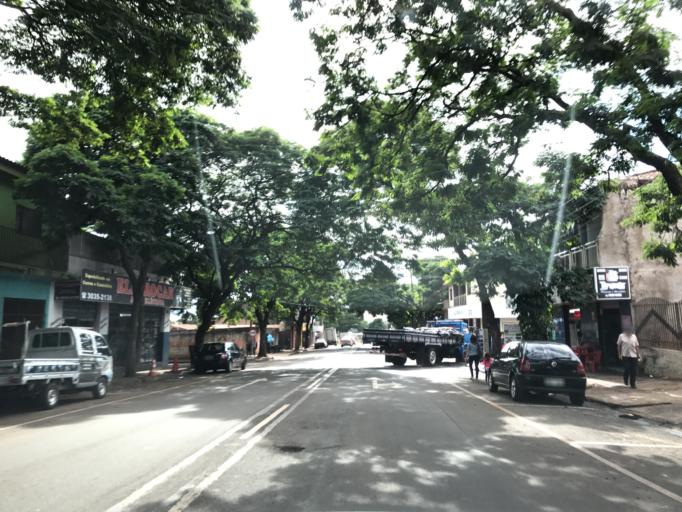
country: BR
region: Parana
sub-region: Sarandi
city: Sarandi
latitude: -23.4351
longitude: -51.8680
